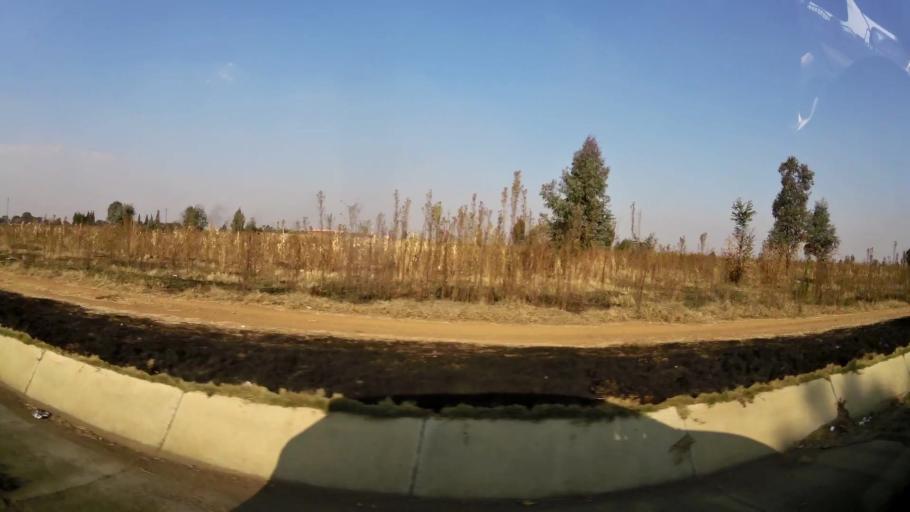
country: ZA
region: Gauteng
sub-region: Ekurhuleni Metropolitan Municipality
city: Benoni
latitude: -26.1403
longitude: 28.3903
